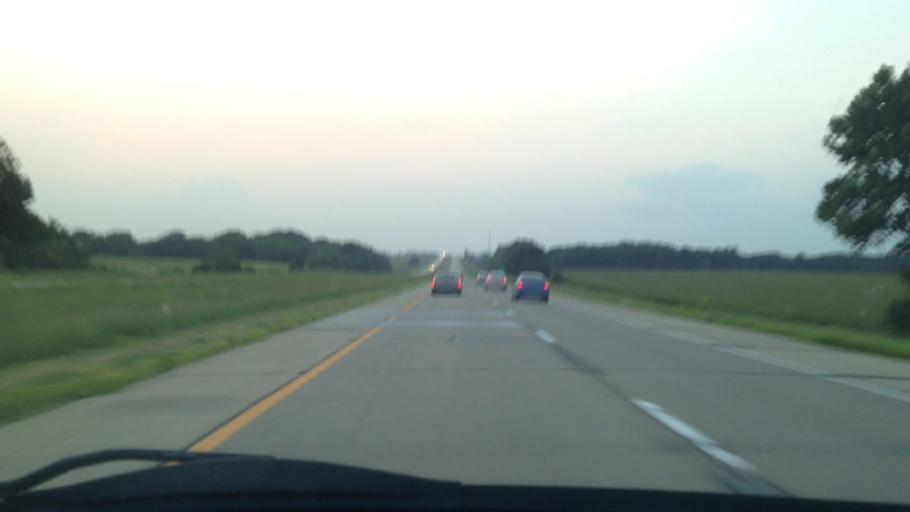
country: US
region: Iowa
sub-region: Benton County
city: Urbana
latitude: 42.2945
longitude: -91.9561
